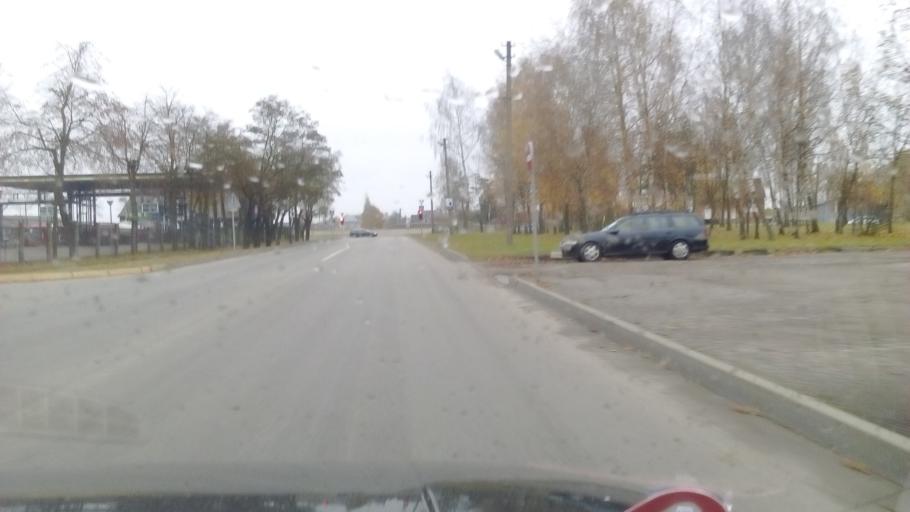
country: LT
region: Marijampoles apskritis
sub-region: Marijampole Municipality
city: Marijampole
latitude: 54.5601
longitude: 23.3630
